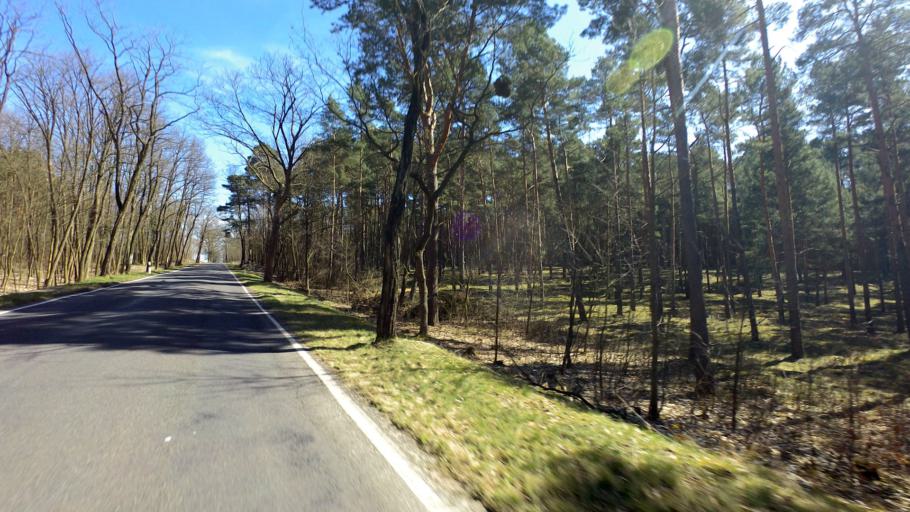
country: DE
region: Brandenburg
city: Munchehofe
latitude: 52.1601
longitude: 13.8838
